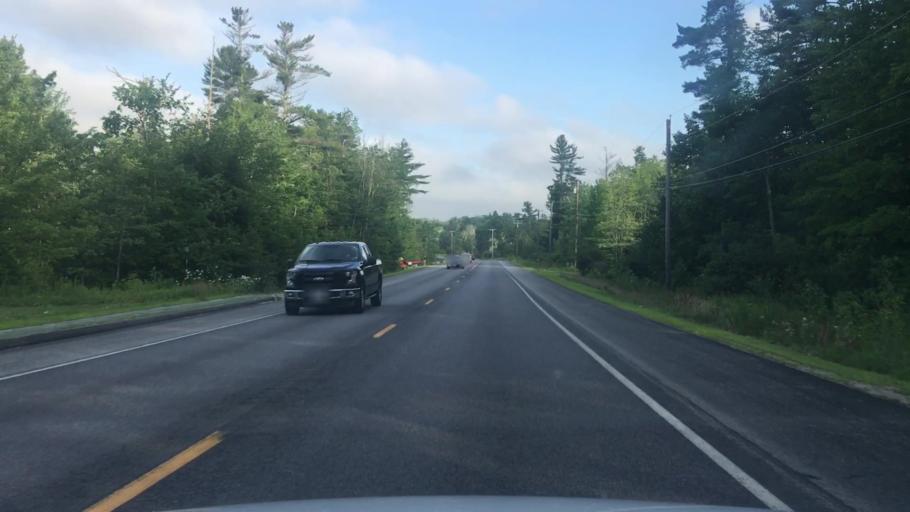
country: US
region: Maine
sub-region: Cumberland County
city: South Windham
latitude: 43.7847
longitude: -70.3921
